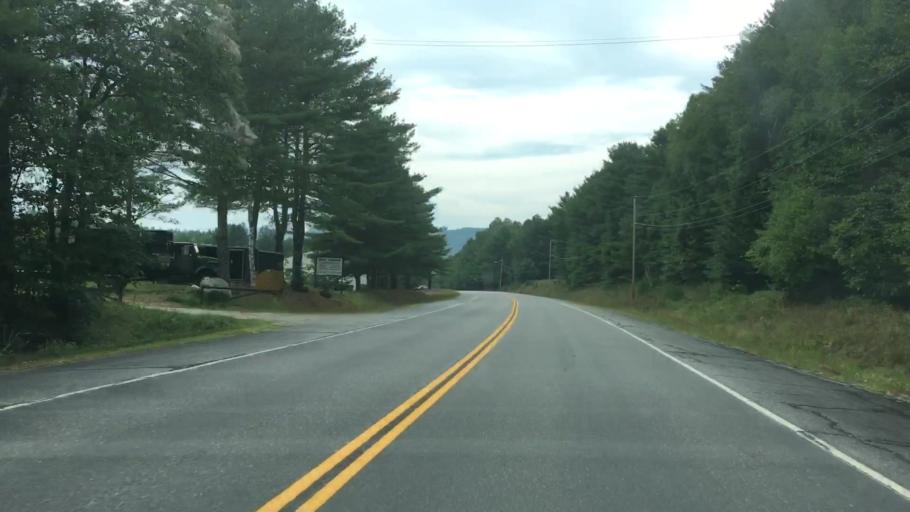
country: US
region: Maine
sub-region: Oxford County
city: Bethel
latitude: 44.4869
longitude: -70.7519
